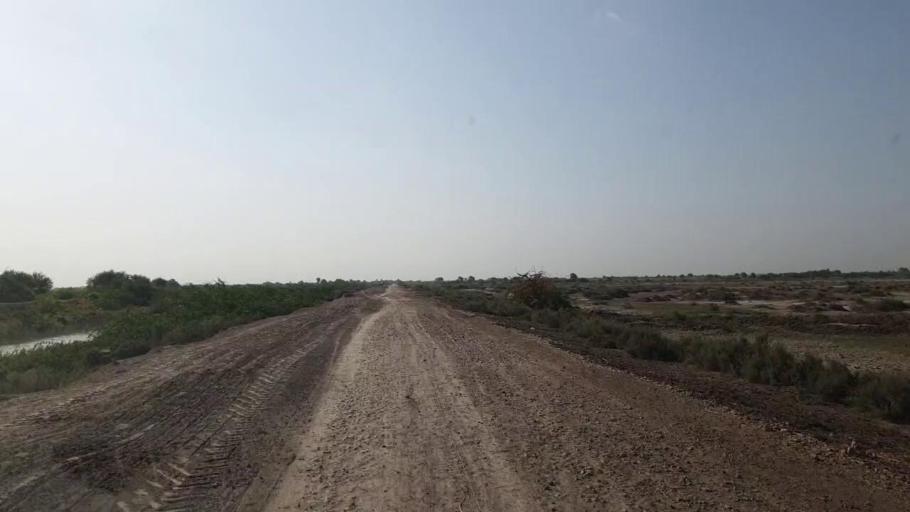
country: PK
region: Sindh
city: Kadhan
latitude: 24.6331
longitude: 69.0727
